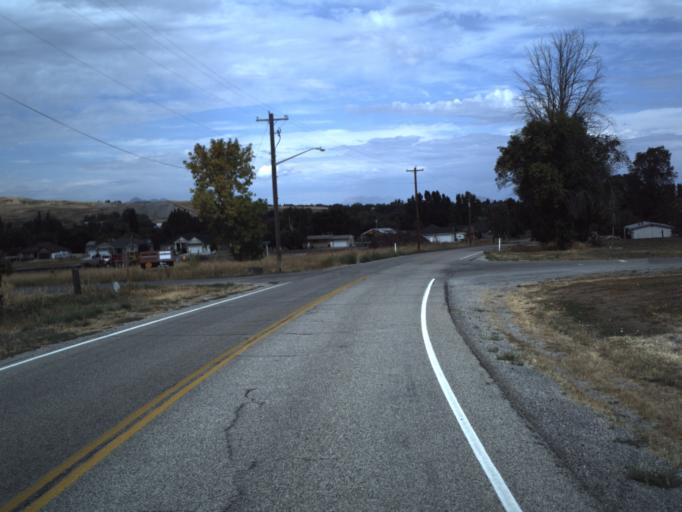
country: US
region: Utah
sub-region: Cache County
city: Wellsville
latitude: 41.6194
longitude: -111.9349
